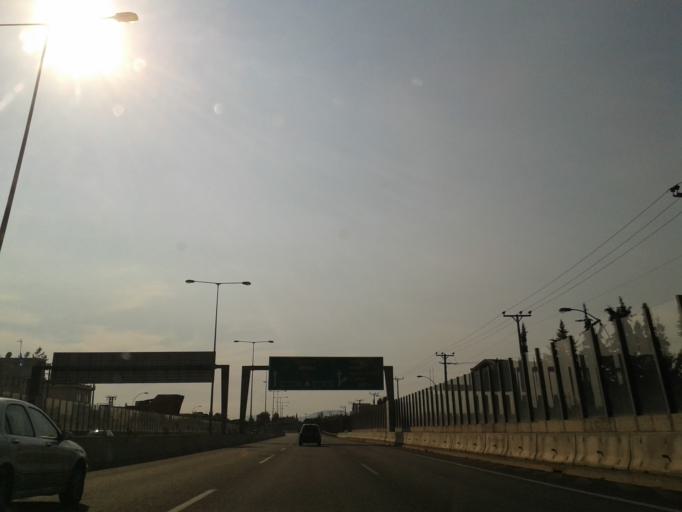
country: GR
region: Attica
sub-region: Nomarchia Athinas
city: Nea Erythraia
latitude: 38.0983
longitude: 23.7999
